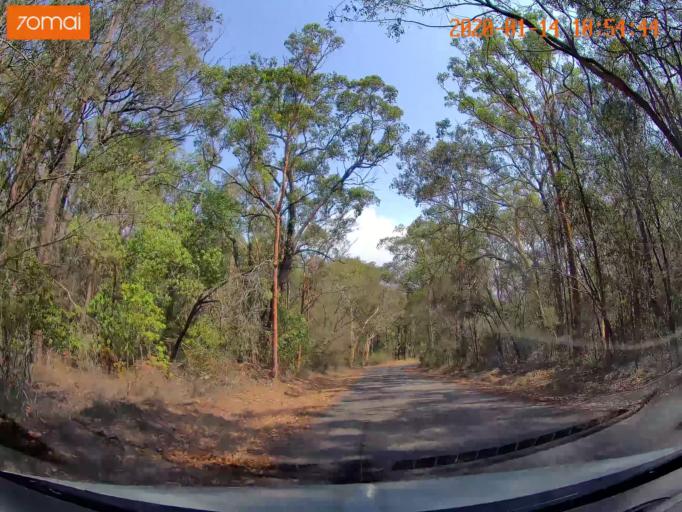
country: AU
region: New South Wales
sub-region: Lake Macquarie Shire
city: Dora Creek
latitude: -33.0976
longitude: 151.4861
